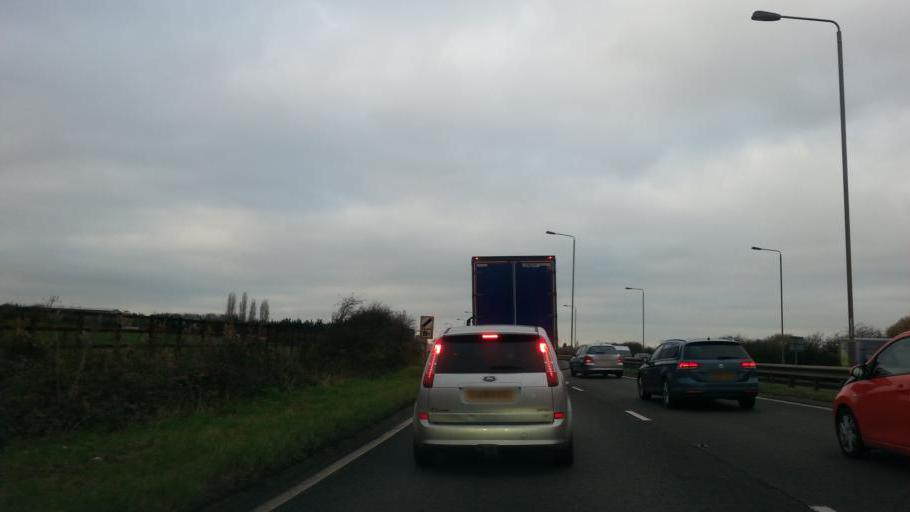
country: GB
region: England
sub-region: Nottinghamshire
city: West Bridgford
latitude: 52.9335
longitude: -1.0951
